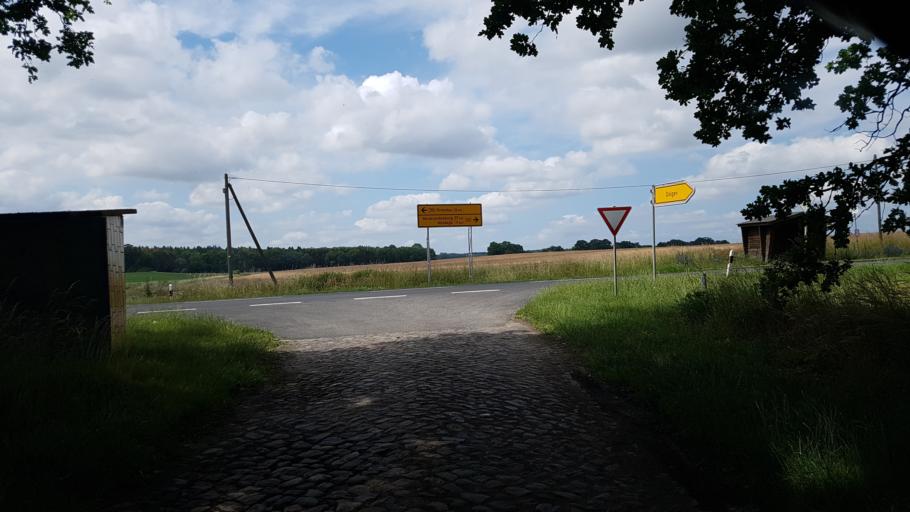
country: DE
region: Mecklenburg-Vorpommern
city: Strasburg
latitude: 53.4158
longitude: 13.7185
